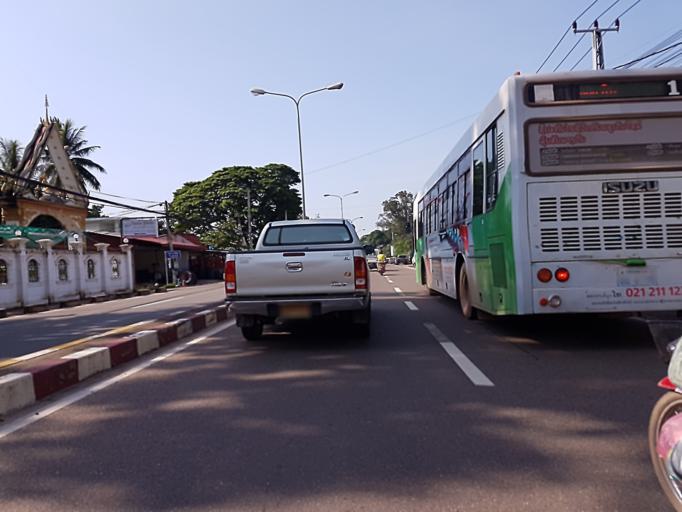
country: LA
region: Vientiane
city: Vientiane
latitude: 17.9361
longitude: 102.6174
